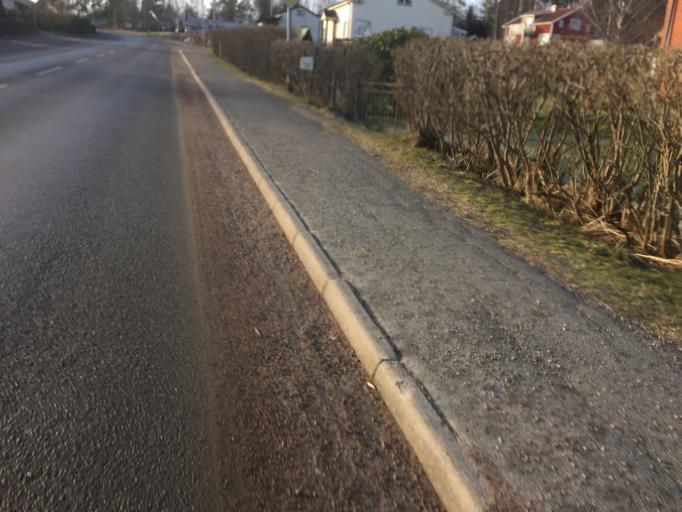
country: SE
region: Joenkoeping
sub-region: Aneby Kommun
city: Aneby
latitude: 57.8466
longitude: 14.8212
